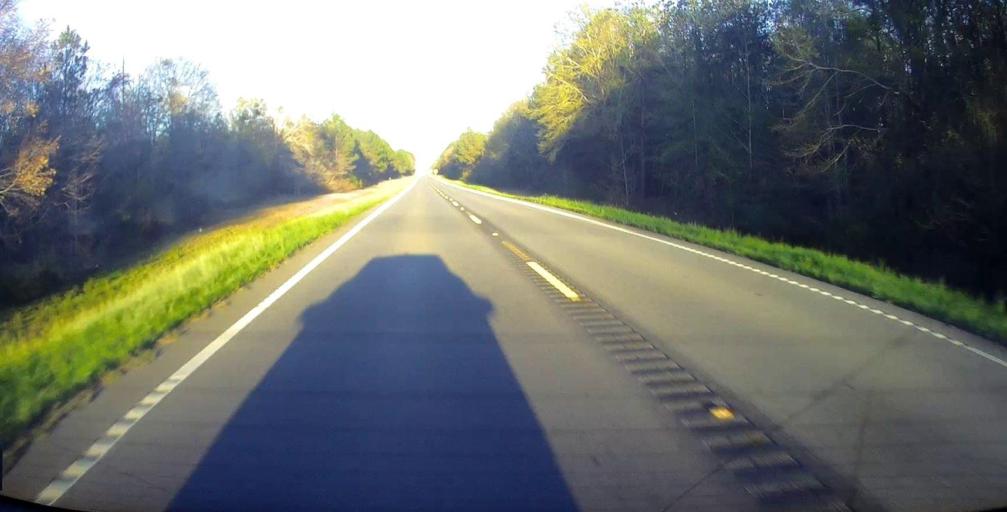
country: US
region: Georgia
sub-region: Crisp County
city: Cordele
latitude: 31.9572
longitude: -83.6197
